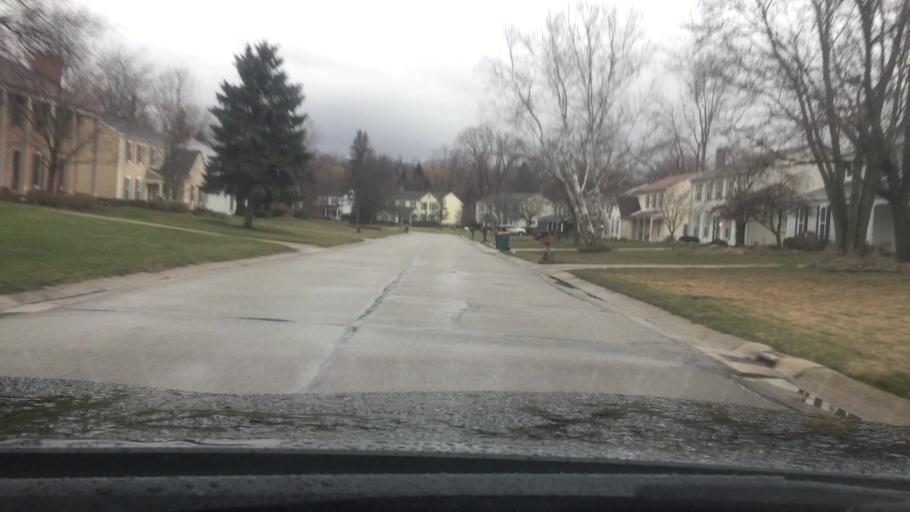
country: US
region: Michigan
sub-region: Oakland County
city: Farmington Hills
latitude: 42.5008
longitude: -83.4070
